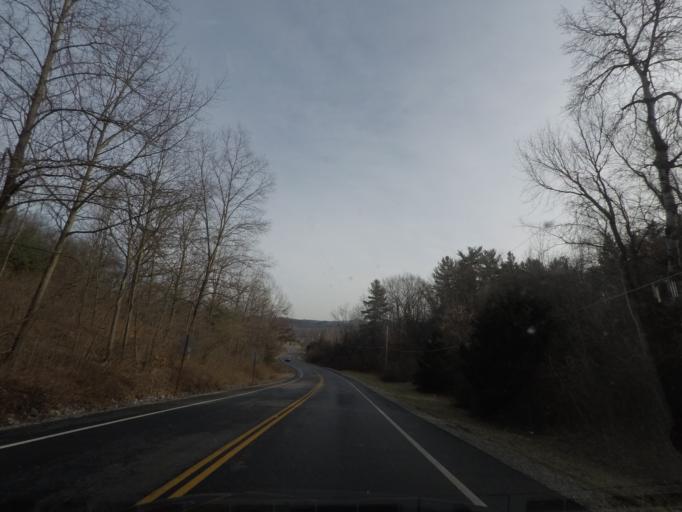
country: US
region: New York
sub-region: Saratoga County
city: Mechanicville
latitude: 42.8610
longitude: -73.6889
